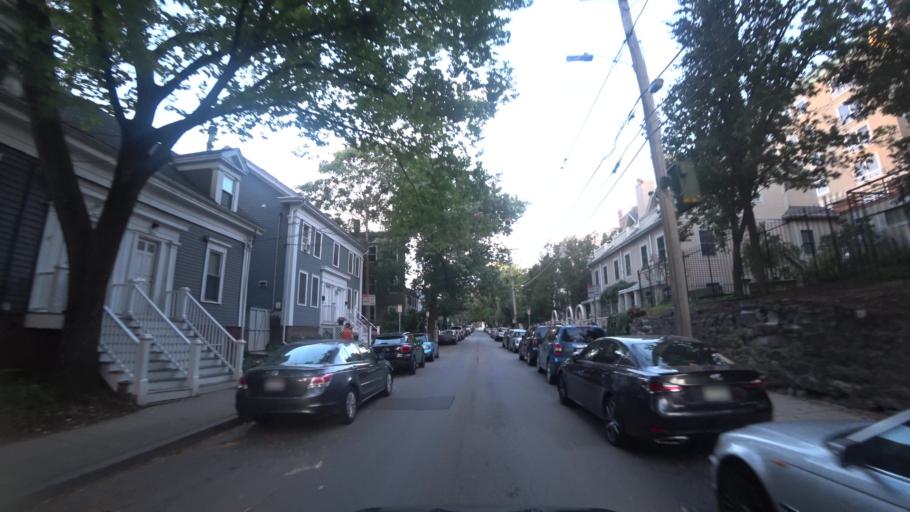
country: US
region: Massachusetts
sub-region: Middlesex County
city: Cambridge
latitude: 42.3686
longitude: -71.1111
